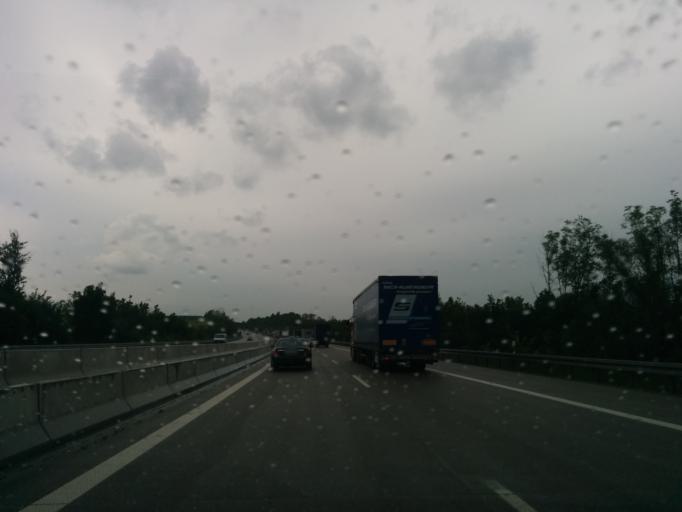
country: DE
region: Bavaria
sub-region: Regierungsbezirk Unterfranken
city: Obernbreit
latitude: 49.6439
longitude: 10.1647
